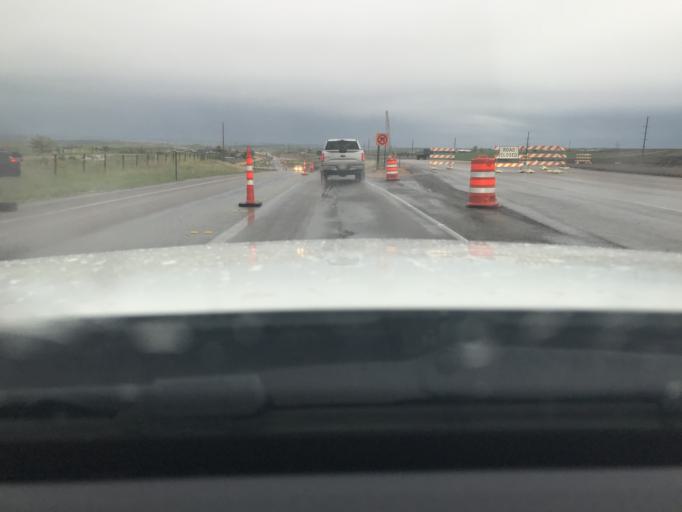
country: US
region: Wyoming
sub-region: Converse County
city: Douglas
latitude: 42.7825
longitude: -105.5201
